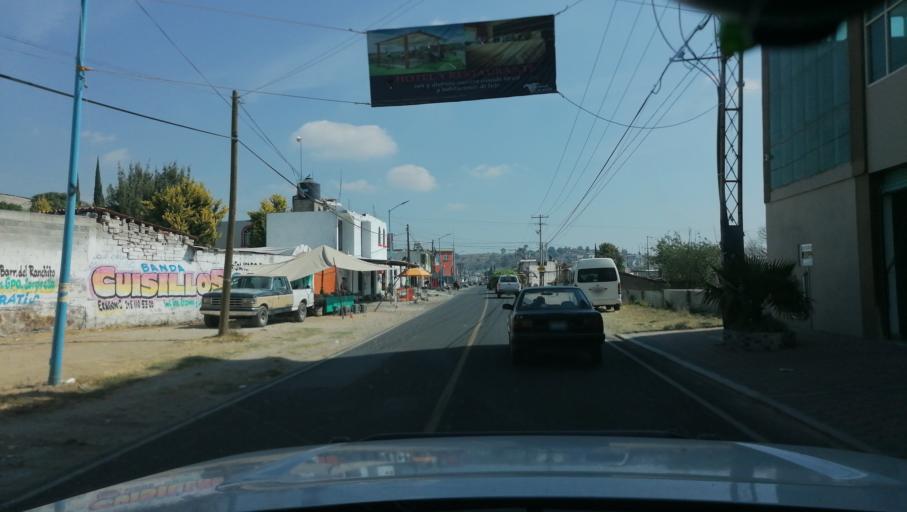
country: MX
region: Tlaxcala
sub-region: Tetlatlahuca
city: Santa Cruz Aquiahuac
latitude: 19.2339
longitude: -98.2855
